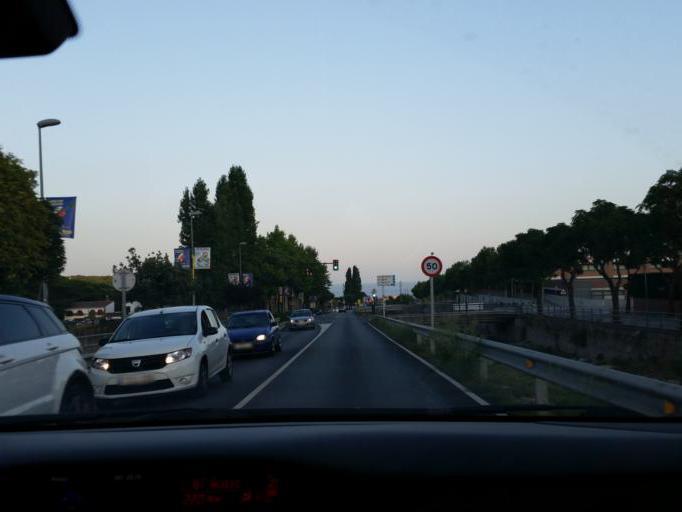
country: ES
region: Catalonia
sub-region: Provincia de Barcelona
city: Cabrils
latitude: 41.5225
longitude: 2.3698
